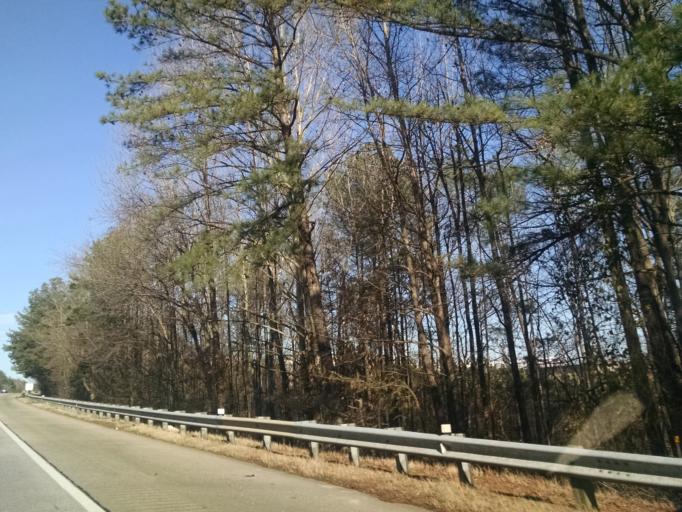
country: US
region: Georgia
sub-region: Gwinnett County
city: Sugar Hill
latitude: 34.0586
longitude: -84.0210
